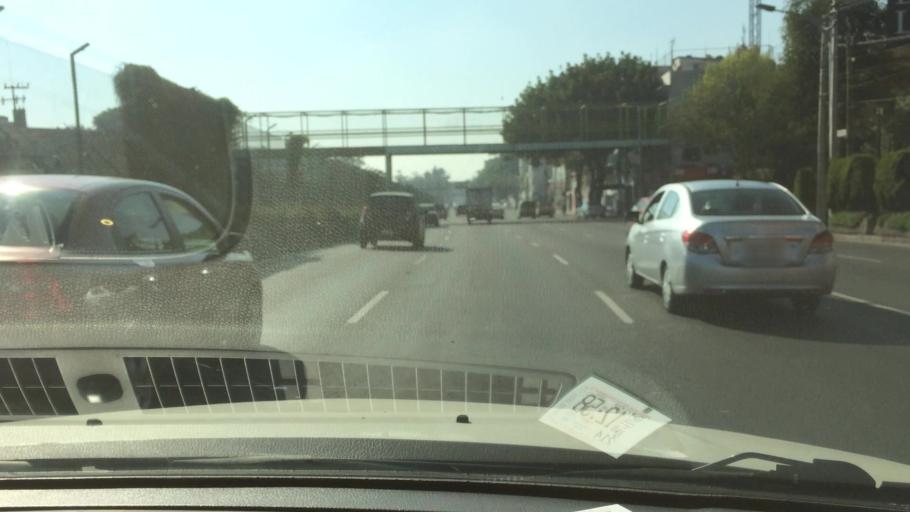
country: MX
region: Mexico City
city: Coyoacan
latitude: 19.3490
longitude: -99.1456
